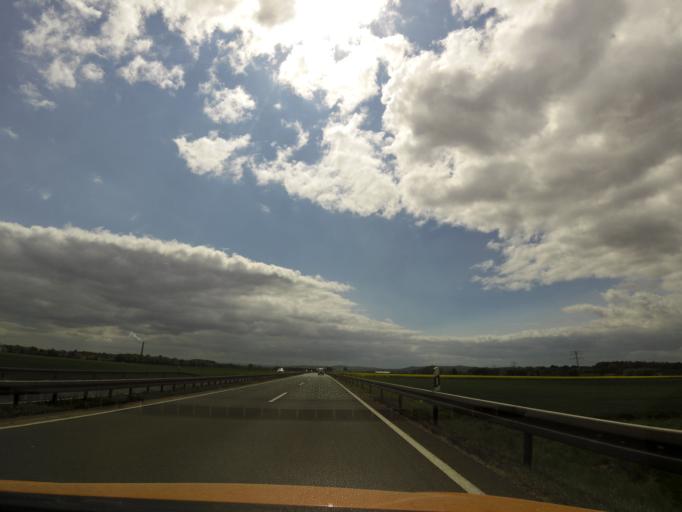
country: DE
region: Lower Saxony
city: Lengede
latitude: 52.1631
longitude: 10.3645
